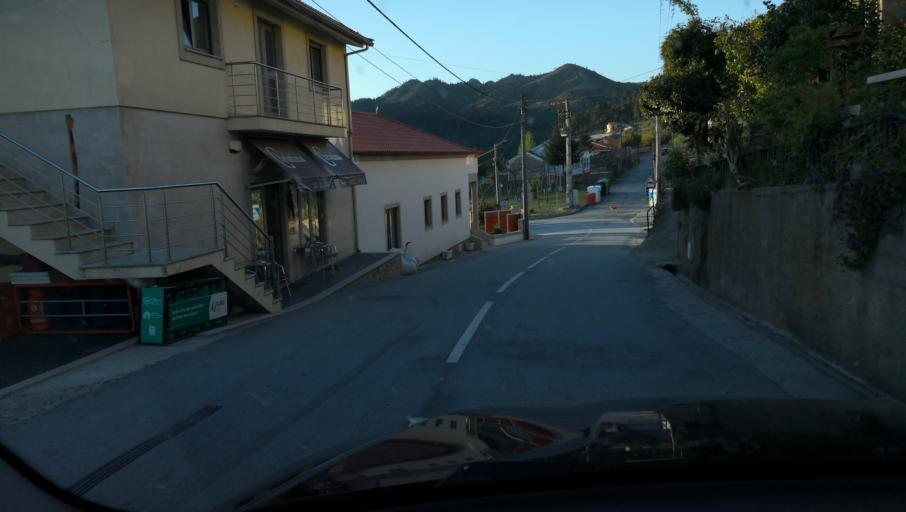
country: PT
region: Vila Real
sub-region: Mondim de Basto
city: Mondim de Basto
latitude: 41.4136
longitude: -7.8788
